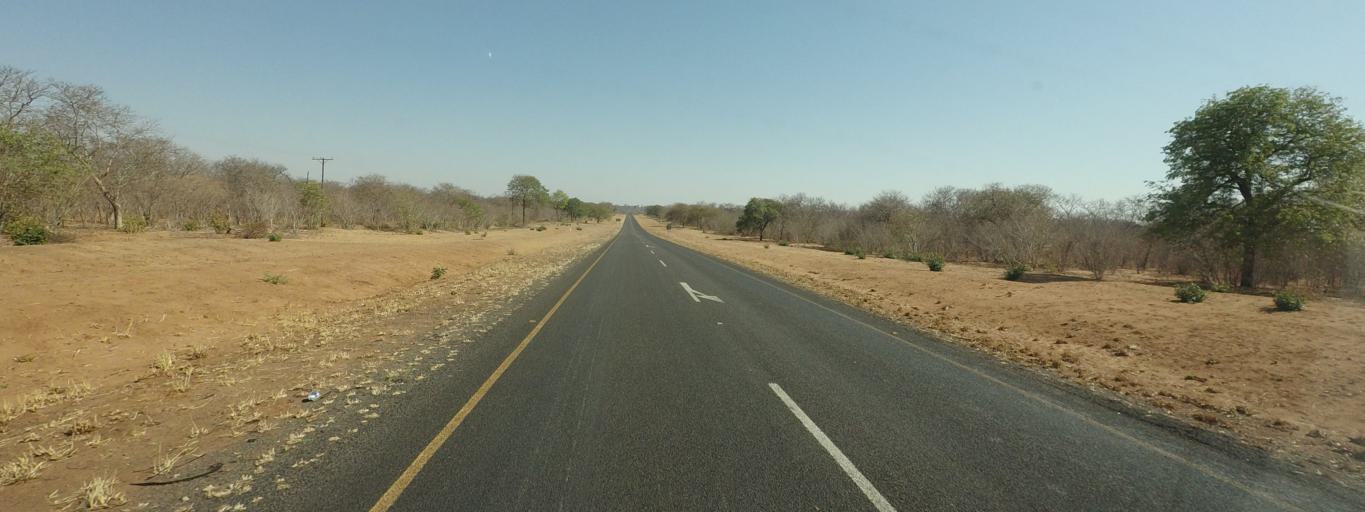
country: BW
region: North West
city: Kasane
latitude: -17.8887
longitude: 25.2145
